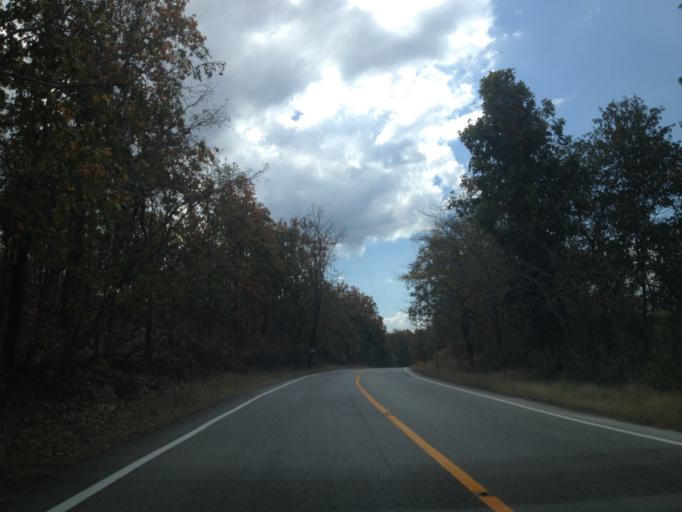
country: TH
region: Chiang Mai
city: Hot
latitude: 18.1712
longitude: 98.4451
